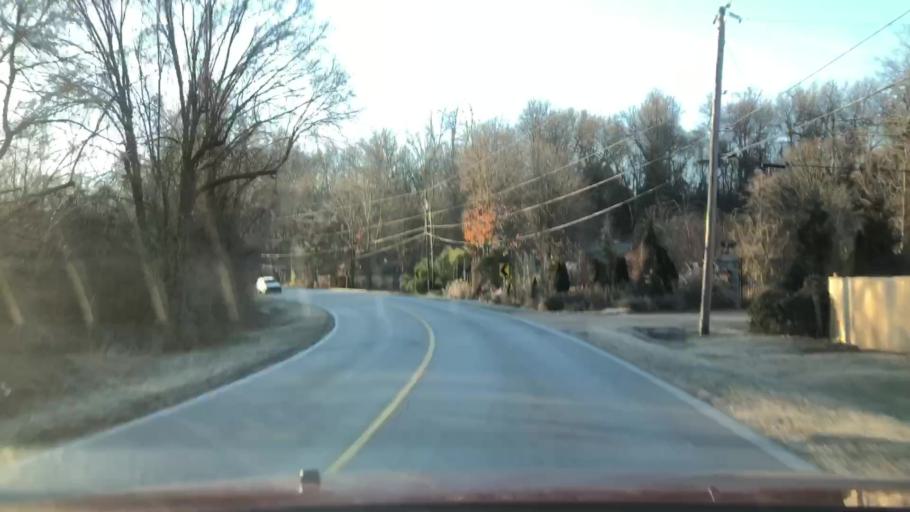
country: US
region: Missouri
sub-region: Greene County
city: Springfield
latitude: 37.1627
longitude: -93.2448
